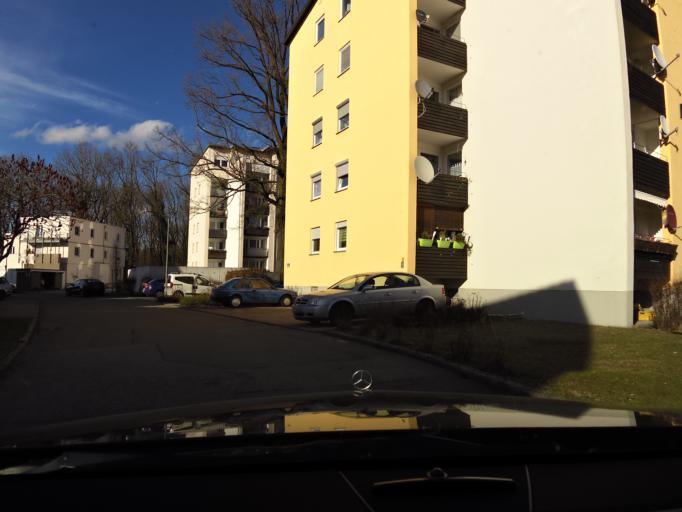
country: DE
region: Bavaria
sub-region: Lower Bavaria
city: Ergolding
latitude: 48.5511
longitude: 12.1787
